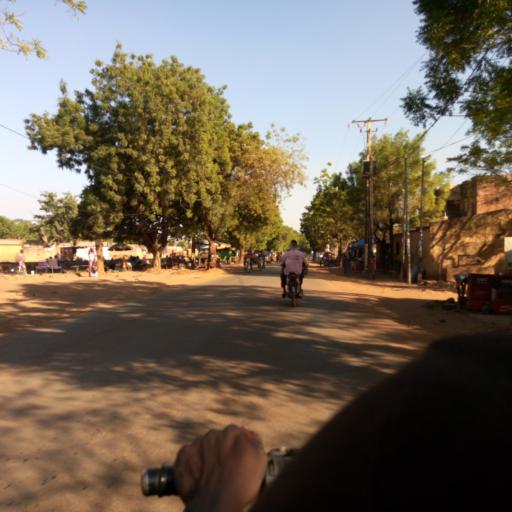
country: ML
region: Bamako
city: Bamako
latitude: 12.6577
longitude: -8.0303
